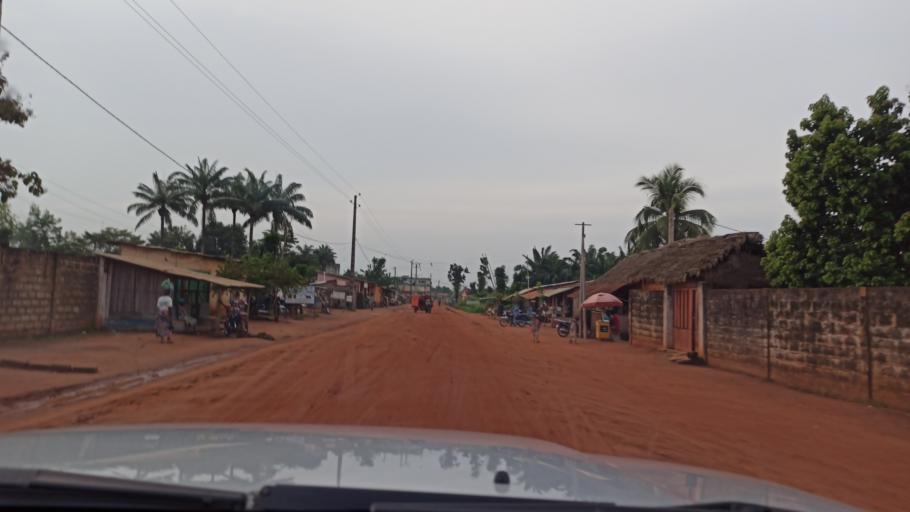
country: BJ
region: Queme
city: Porto-Novo
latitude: 6.5204
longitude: 2.6750
